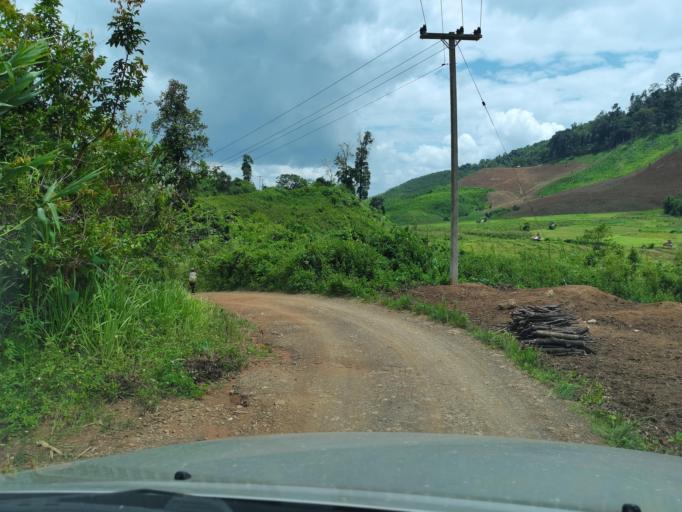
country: LA
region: Loungnamtha
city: Muang Long
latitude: 20.7312
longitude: 101.0142
